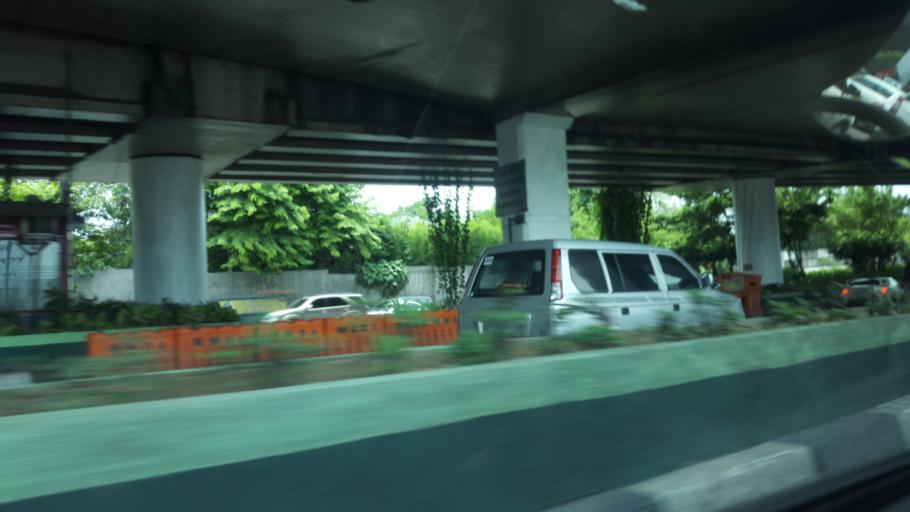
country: PH
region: Metro Manila
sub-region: Makati City
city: Makati City
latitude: 14.5555
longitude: 121.0356
